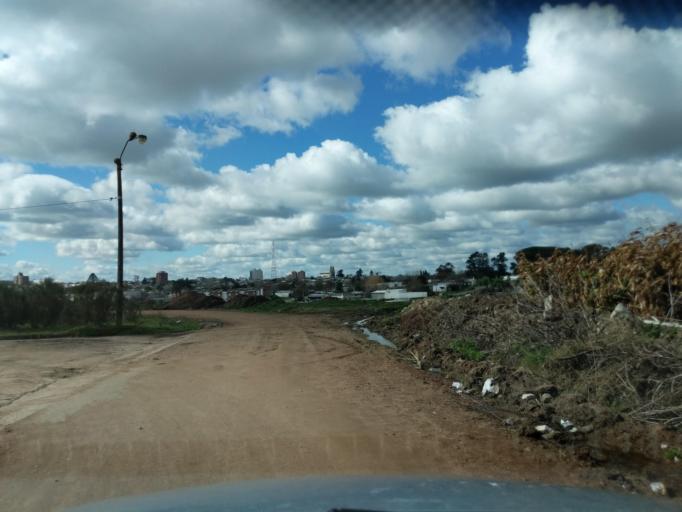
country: UY
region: Florida
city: Florida
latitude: -34.0957
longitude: -56.2307
